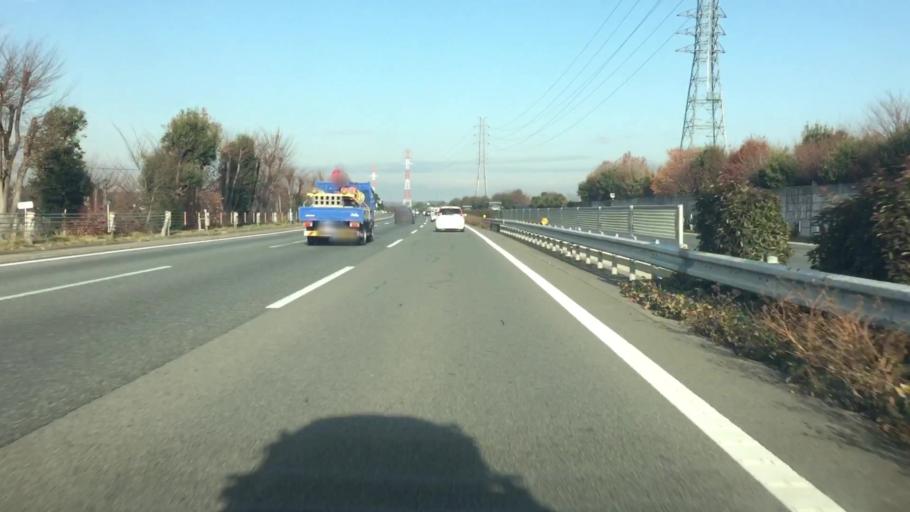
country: JP
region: Saitama
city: Yorii
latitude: 36.1541
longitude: 139.2172
